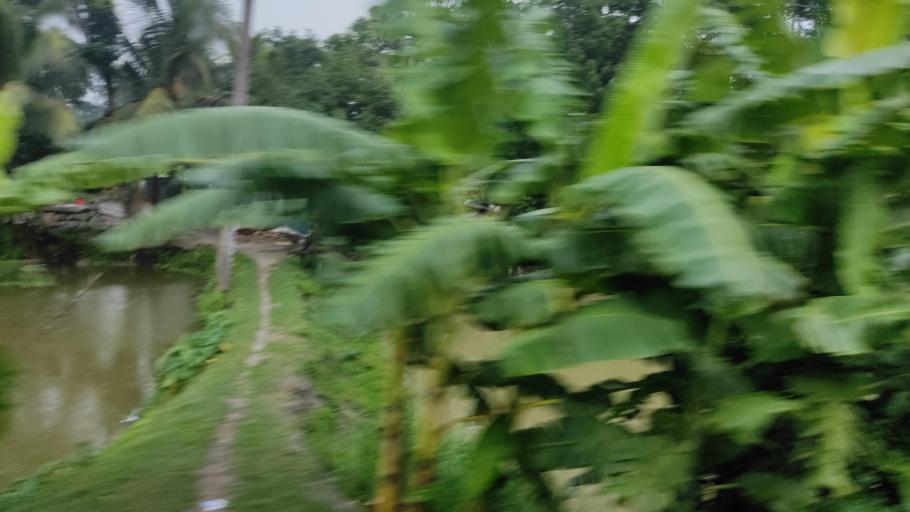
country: BD
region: Barisal
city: Bhandaria
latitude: 22.3130
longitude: 90.3252
